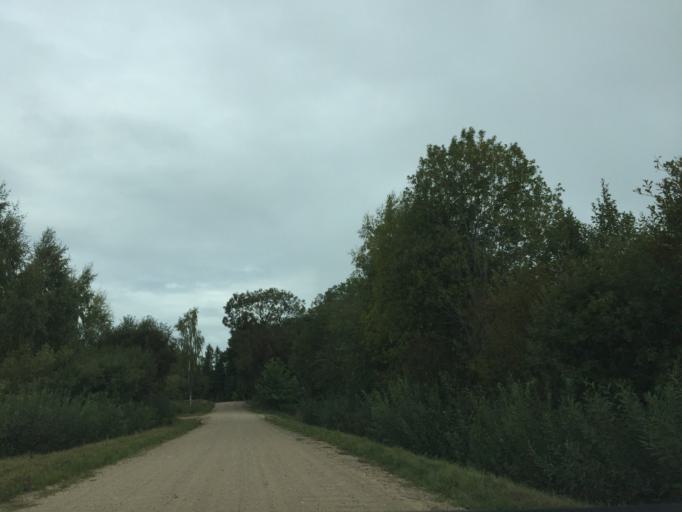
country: LV
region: Limbazu Rajons
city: Limbazi
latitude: 57.5249
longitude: 24.9116
